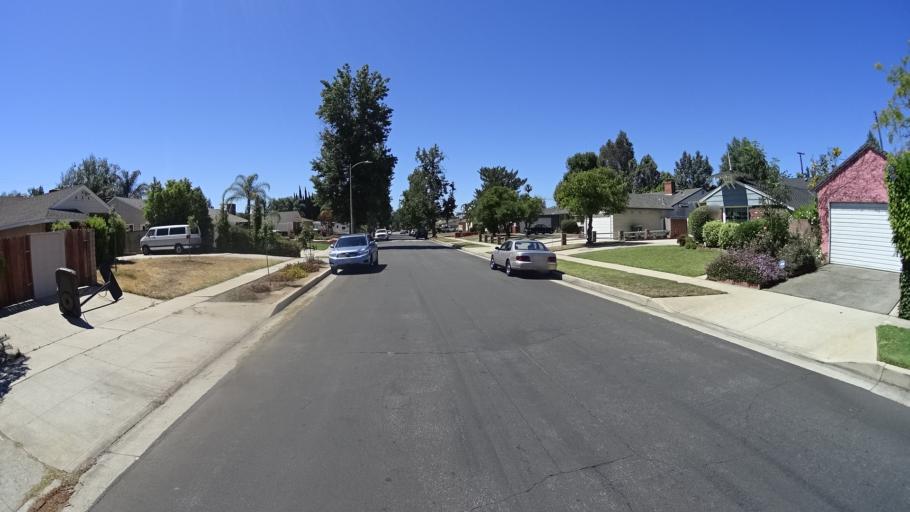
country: US
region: California
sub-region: Los Angeles County
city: San Fernando
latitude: 34.2560
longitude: -118.4610
